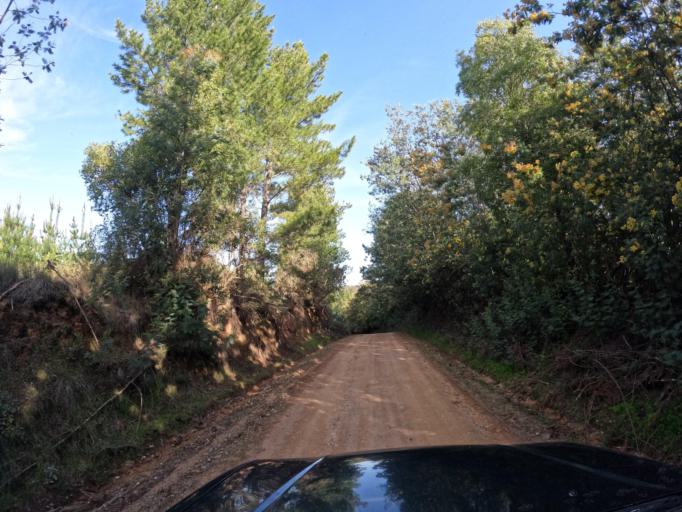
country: CL
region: Biobio
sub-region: Provincia de Biobio
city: La Laja
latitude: -37.1258
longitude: -72.7352
